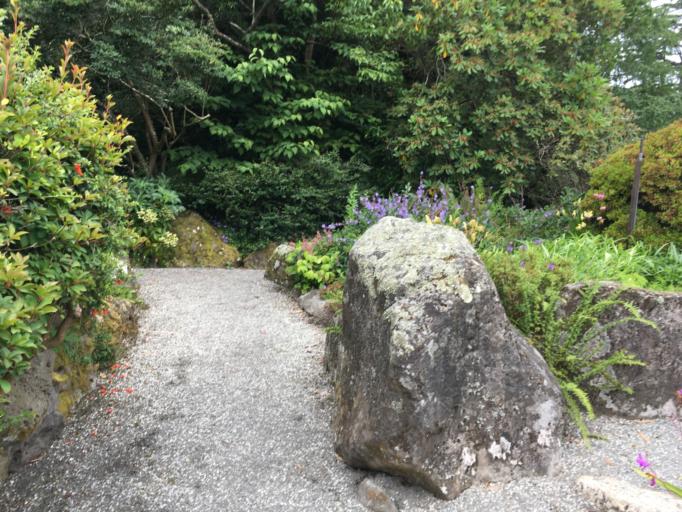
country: NZ
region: Canterbury
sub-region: Christchurch City
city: Christchurch
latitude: -43.5316
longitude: 172.6204
